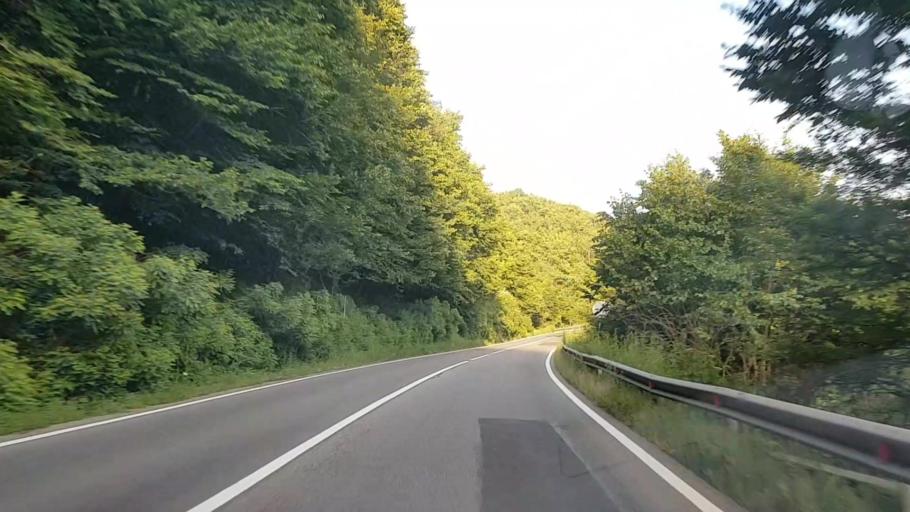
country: RO
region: Harghita
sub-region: Comuna Corund
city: Corund
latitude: 46.4493
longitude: 25.2234
